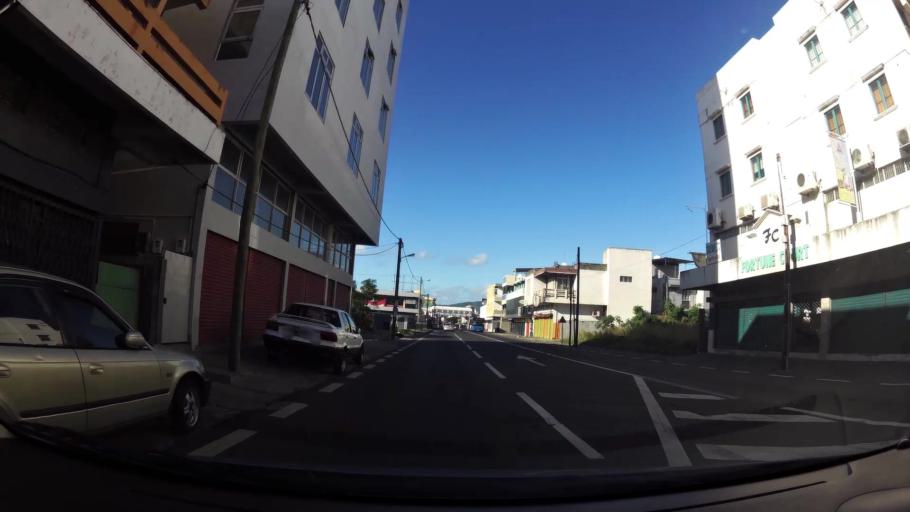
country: MU
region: Port Louis
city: Port Louis
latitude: -20.1671
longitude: 57.4875
